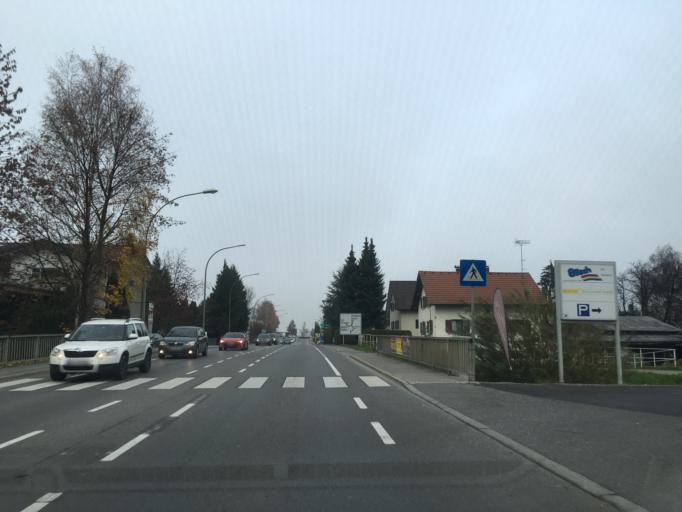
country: AT
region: Vorarlberg
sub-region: Politischer Bezirk Dornbirn
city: Lustenau
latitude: 47.4478
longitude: 9.6646
